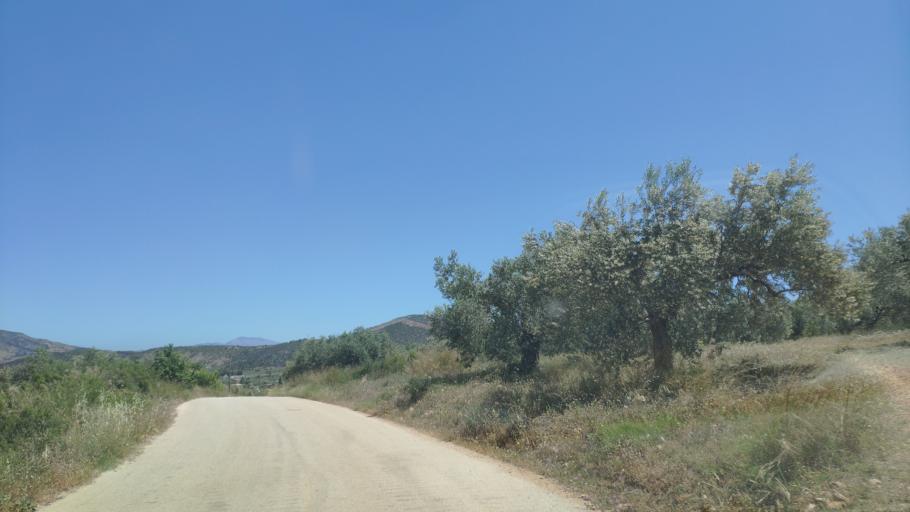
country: GR
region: Peloponnese
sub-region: Nomos Korinthias
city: Athikia
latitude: 37.8107
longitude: 22.9184
